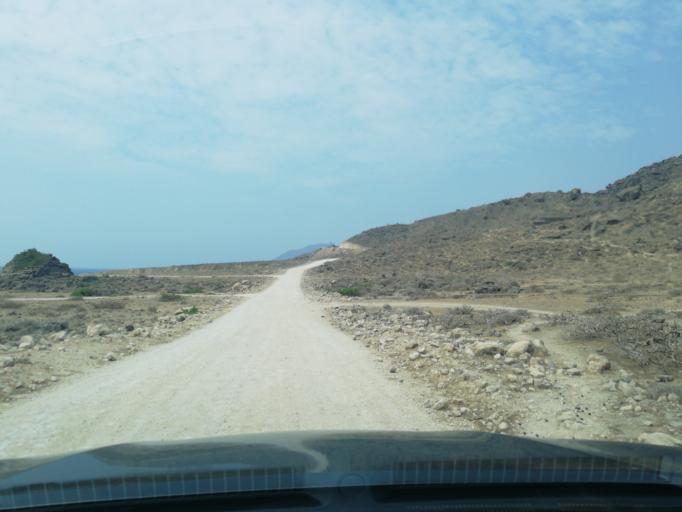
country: OM
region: Zufar
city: Salalah
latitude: 16.8230
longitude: 53.6984
